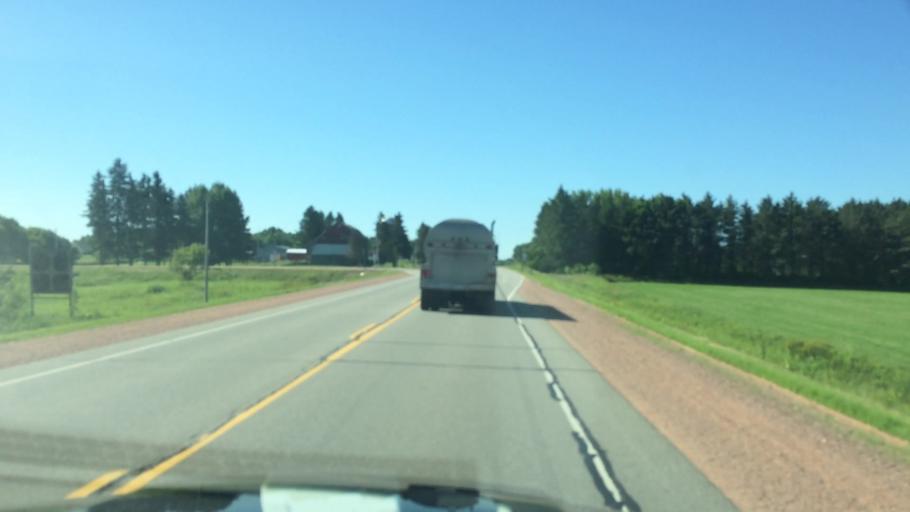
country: US
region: Wisconsin
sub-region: Marathon County
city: Stratford
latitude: 44.7443
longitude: -90.0794
